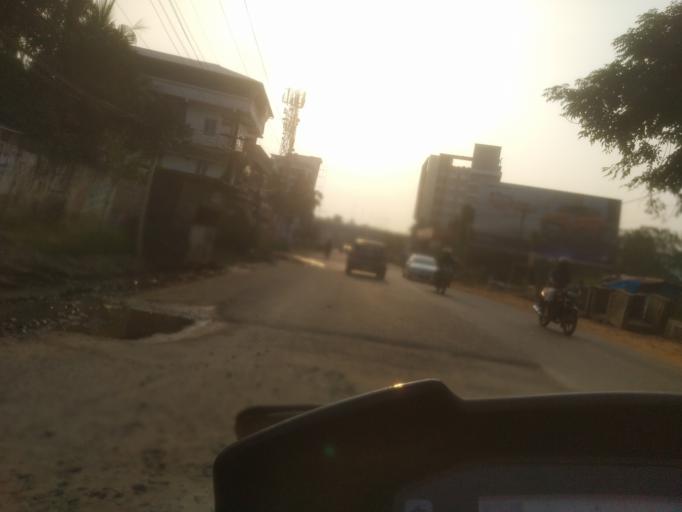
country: IN
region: Kerala
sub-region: Ernakulam
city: Cochin
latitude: 9.9373
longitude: 76.3200
